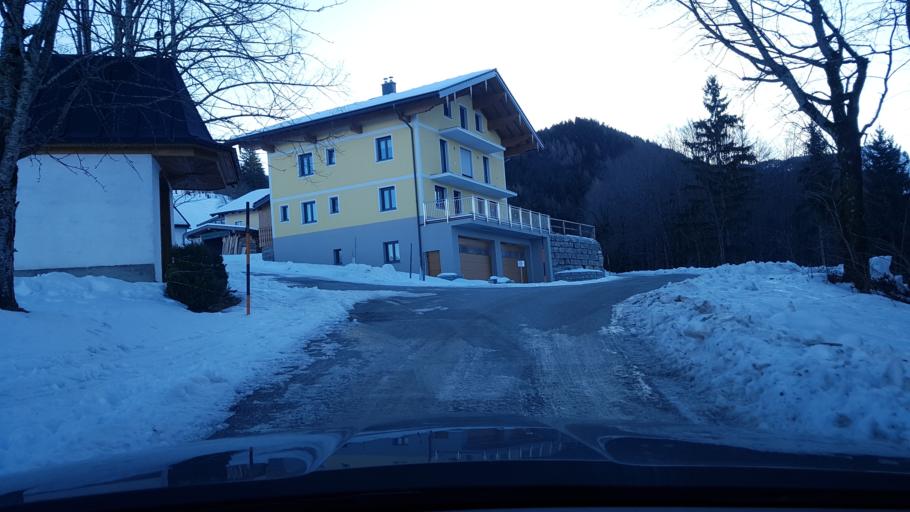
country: AT
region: Salzburg
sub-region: Politischer Bezirk Hallein
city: Scheffau am Tennengebirge
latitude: 47.6472
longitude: 13.2358
